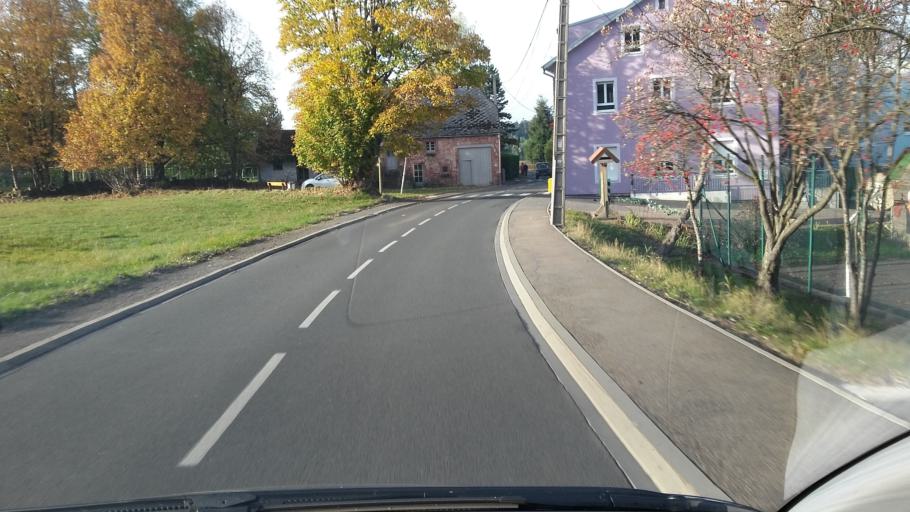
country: FR
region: Lorraine
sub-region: Departement de la Moselle
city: Dabo
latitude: 48.6545
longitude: 7.2694
